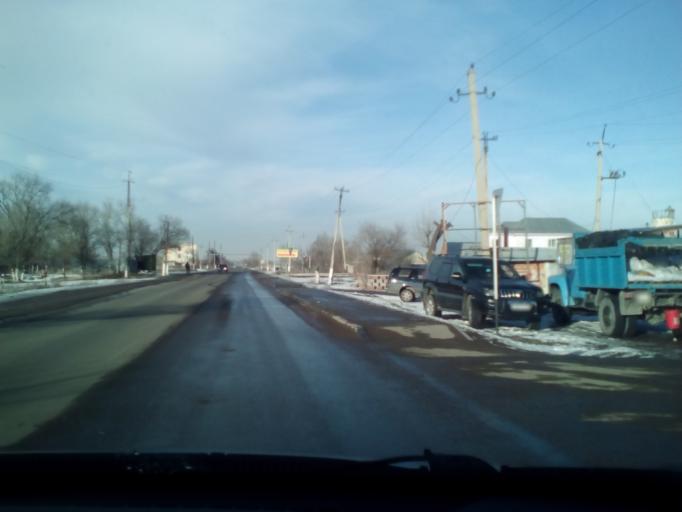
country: KZ
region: Almaty Oblysy
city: Burunday
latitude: 43.1891
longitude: 76.4148
